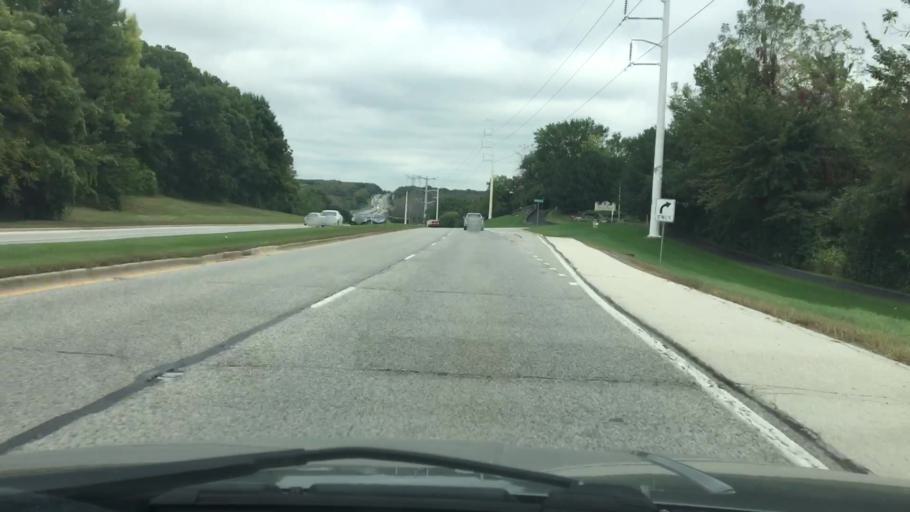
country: US
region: Illinois
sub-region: DuPage County
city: Woodridge
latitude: 41.7492
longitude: -88.0800
